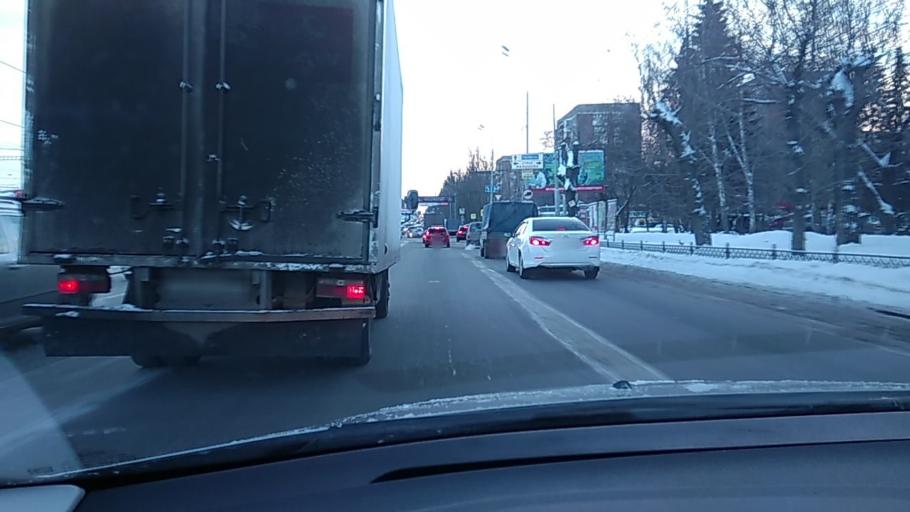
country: RU
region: Sverdlovsk
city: Yekaterinburg
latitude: 56.8386
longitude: 60.6330
